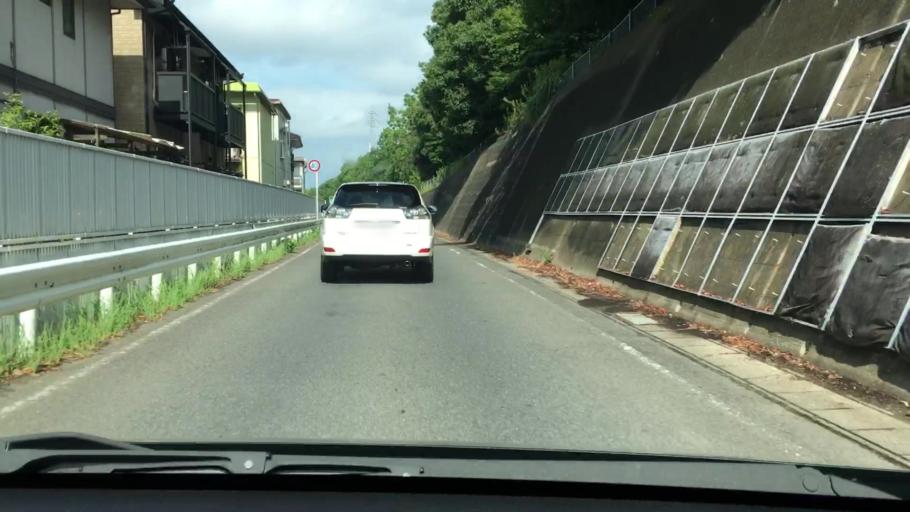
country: JP
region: Nagasaki
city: Sasebo
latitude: 33.1511
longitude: 129.7646
